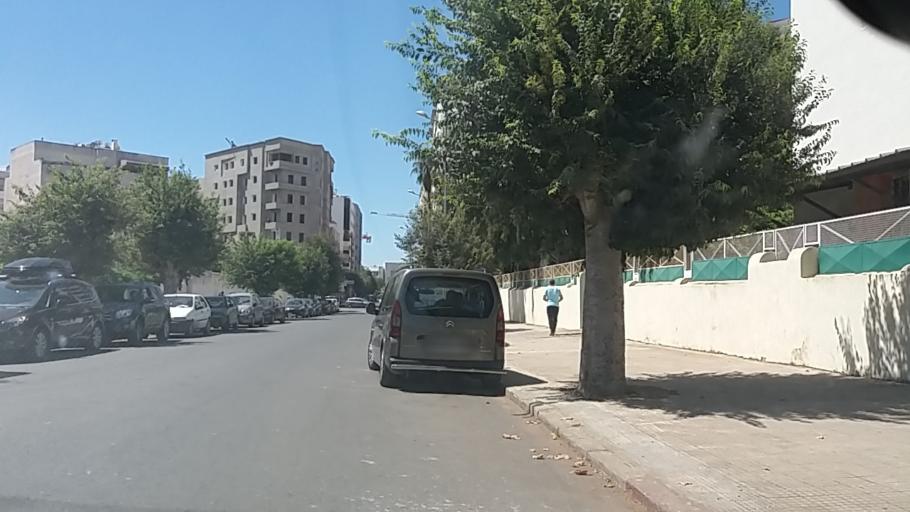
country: MA
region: Gharb-Chrarda-Beni Hssen
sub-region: Kenitra Province
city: Kenitra
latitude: 34.2557
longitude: -6.5804
